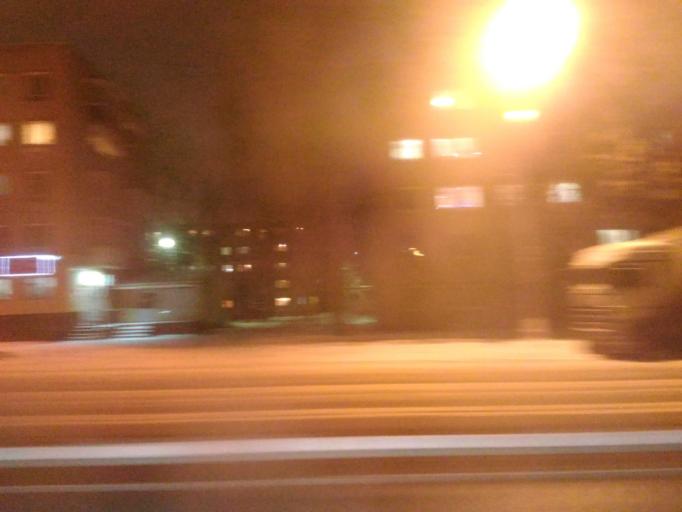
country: RU
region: Ulyanovsk
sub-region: Ulyanovskiy Rayon
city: Ulyanovsk
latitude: 54.3471
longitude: 48.3706
